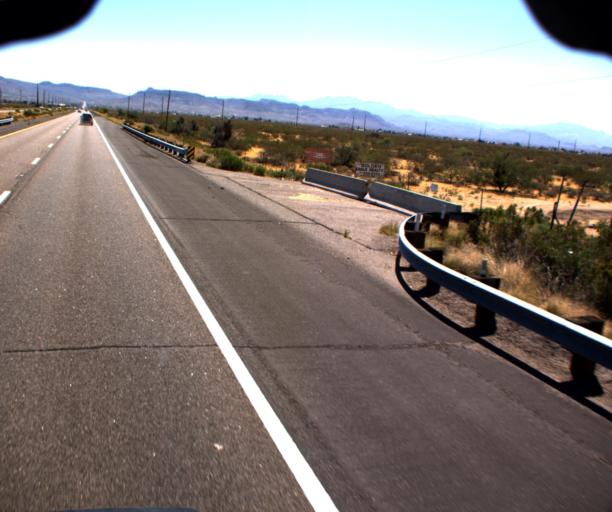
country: US
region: Arizona
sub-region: Mohave County
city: Golden Valley
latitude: 35.2232
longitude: -114.2432
